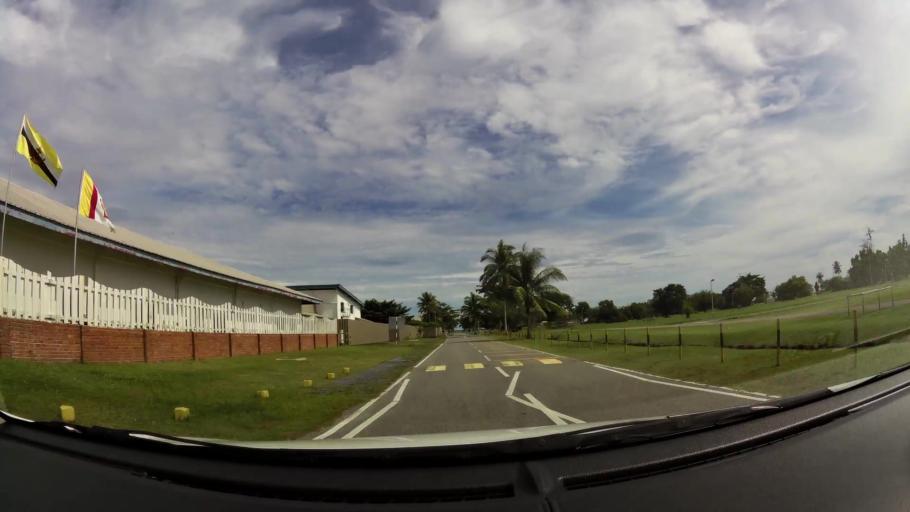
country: BN
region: Belait
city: Seria
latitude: 4.6147
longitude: 114.3219
